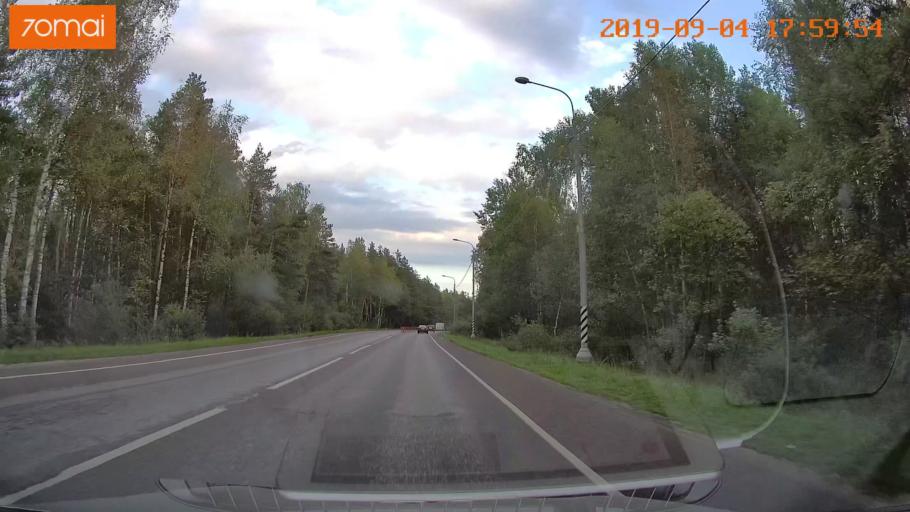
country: RU
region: Moskovskaya
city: Il'inskiy Pogost
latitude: 55.4920
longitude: 38.8508
